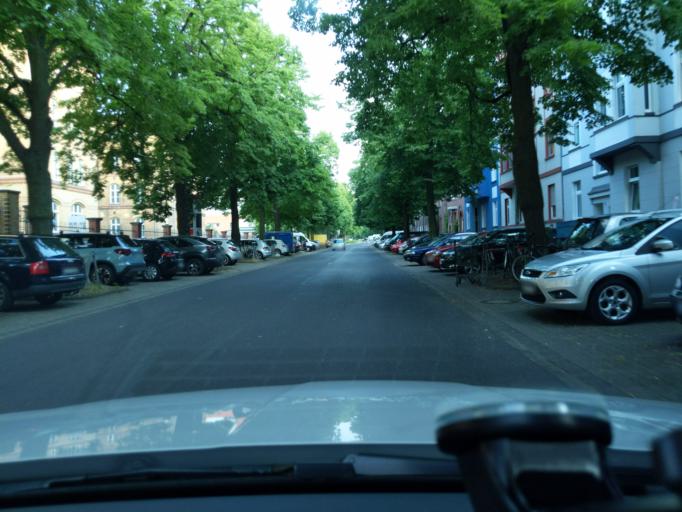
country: DE
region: North Rhine-Westphalia
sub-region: Regierungsbezirk Dusseldorf
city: Dusseldorf
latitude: 51.1974
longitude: 6.7830
